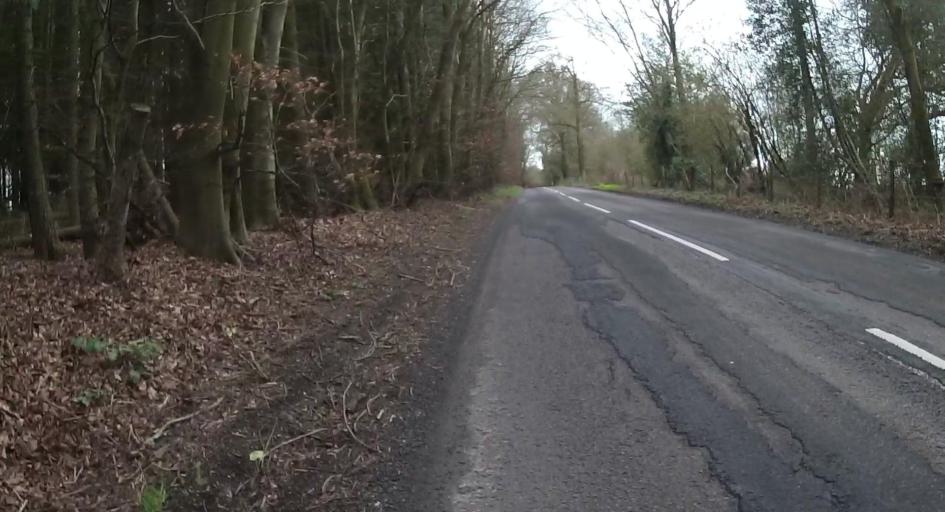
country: GB
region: England
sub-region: Hampshire
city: Alton
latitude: 51.1800
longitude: -0.9841
